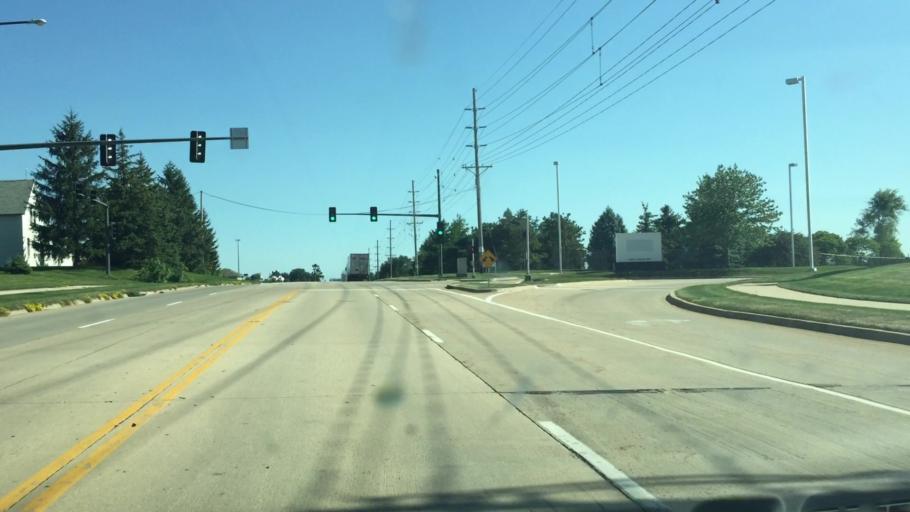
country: US
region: Iowa
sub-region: Linn County
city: Ely
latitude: 41.9188
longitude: -91.6373
